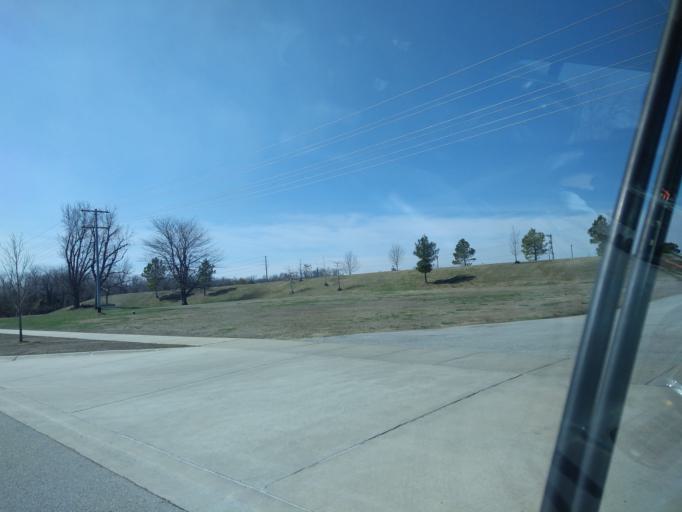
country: US
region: Arkansas
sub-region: Washington County
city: Farmington
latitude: 36.0641
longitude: -94.2312
